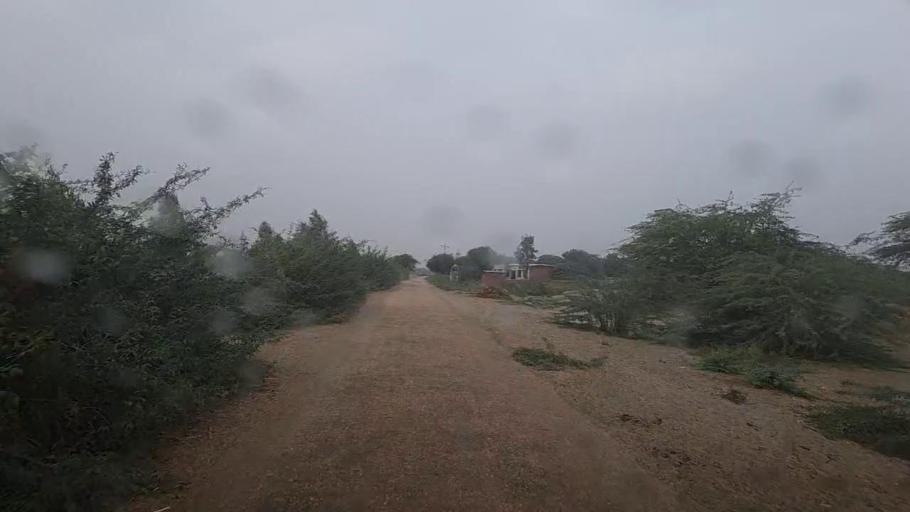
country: PK
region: Sindh
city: Gambat
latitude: 27.3646
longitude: 68.5880
